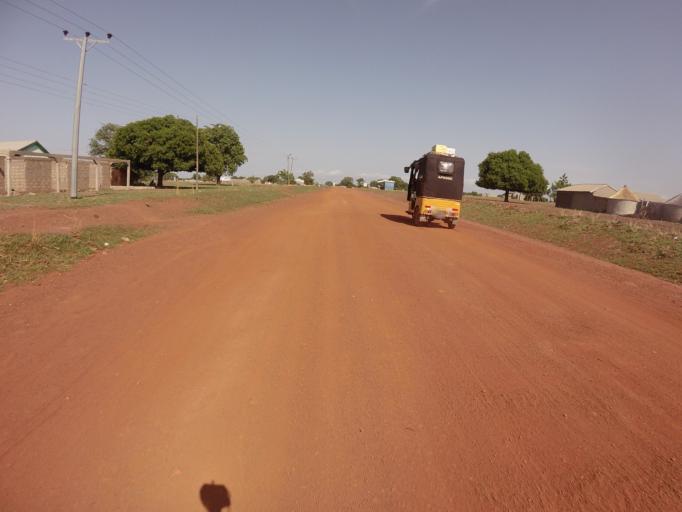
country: GH
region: Upper East
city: Bawku
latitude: 10.8335
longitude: -0.1732
